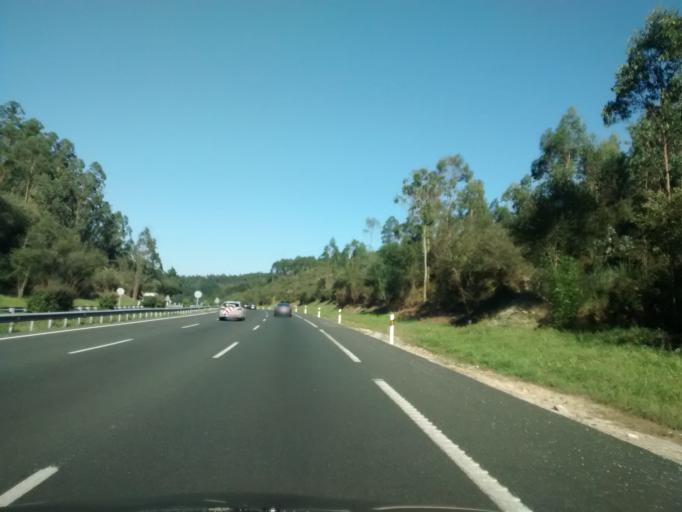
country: ES
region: Cantabria
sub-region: Provincia de Cantabria
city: Luzmela
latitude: 43.3240
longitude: -4.1701
